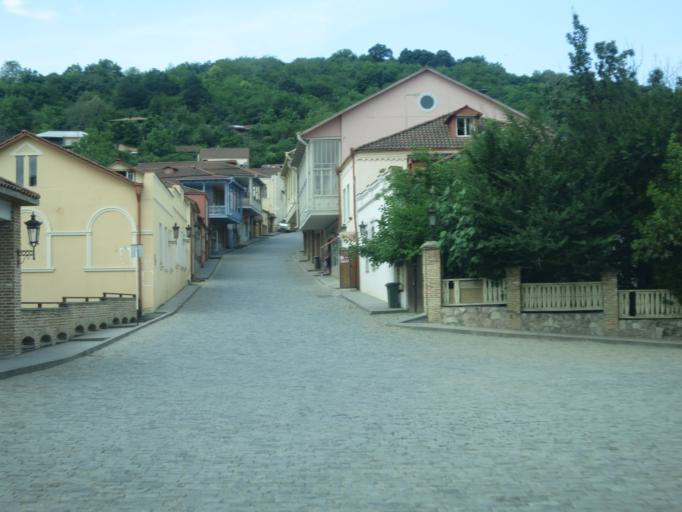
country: GE
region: Kakheti
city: Sighnaghi
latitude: 41.6168
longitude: 45.9209
